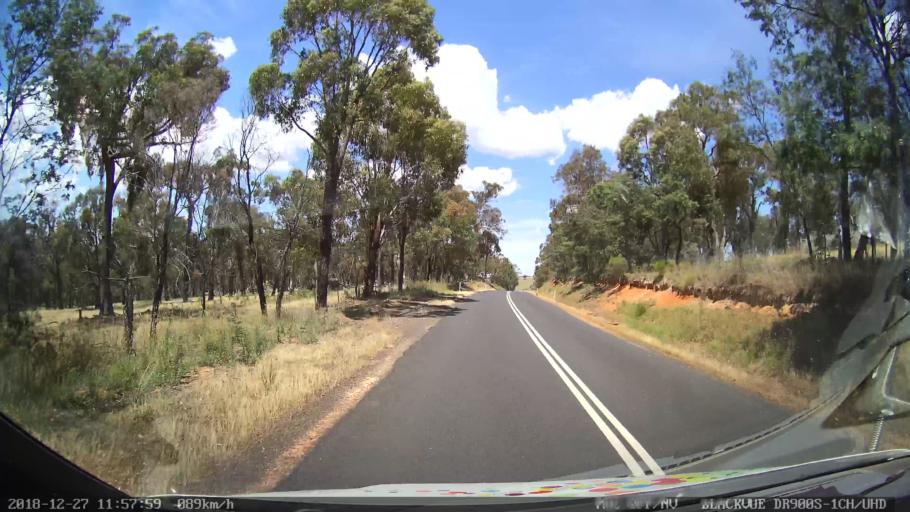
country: AU
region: New South Wales
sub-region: Blayney
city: Blayney
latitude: -33.7186
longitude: 149.3875
